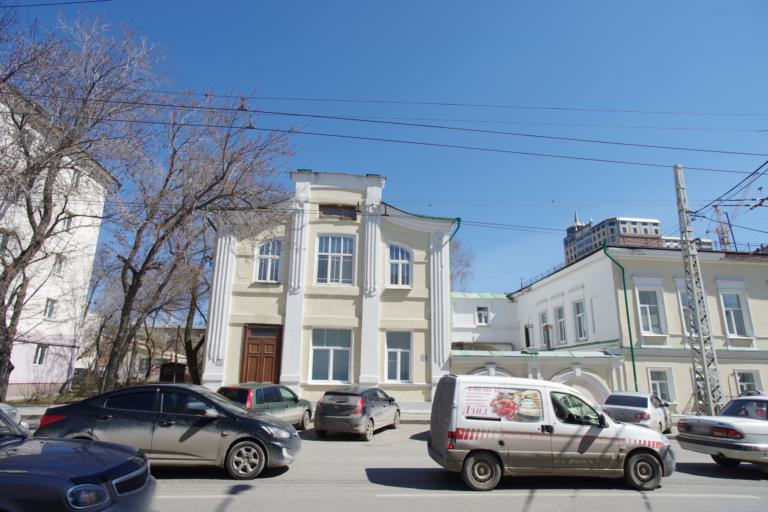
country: RU
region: Sverdlovsk
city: Yekaterinburg
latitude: 56.8242
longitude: 60.6143
